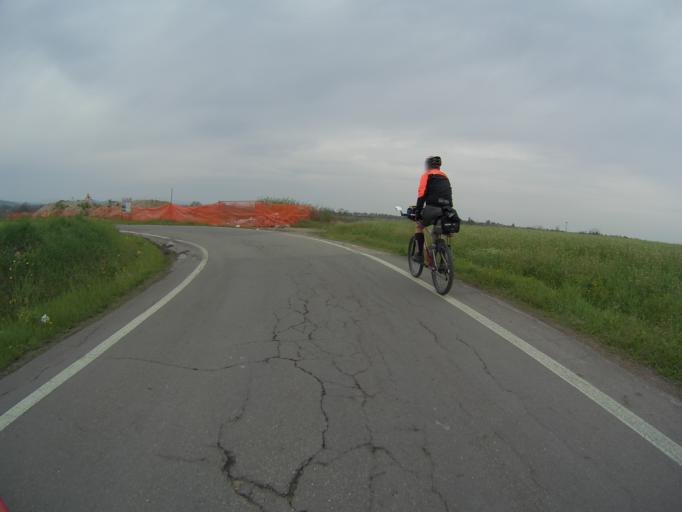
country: IT
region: Emilia-Romagna
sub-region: Provincia di Reggio Emilia
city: Bibbiano
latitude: 44.6560
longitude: 10.4919
